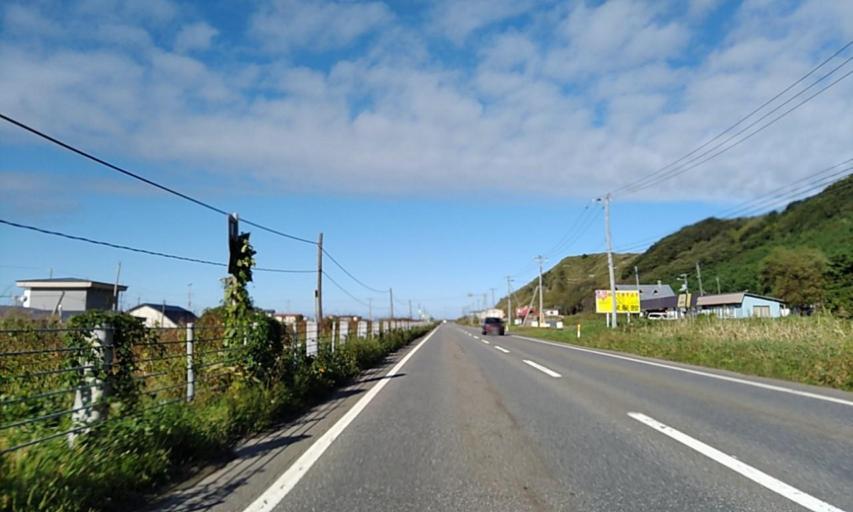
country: JP
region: Hokkaido
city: Shizunai-furukawacho
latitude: 42.3106
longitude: 142.4112
